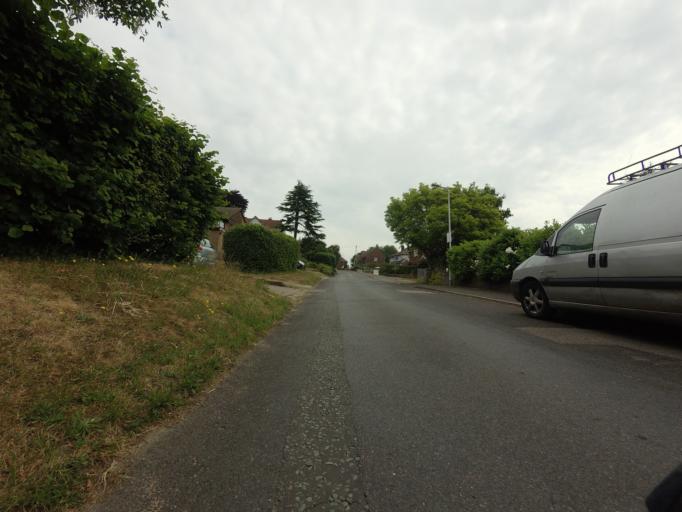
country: GB
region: England
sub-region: Kent
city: Swanley
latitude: 51.3919
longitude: 0.1889
